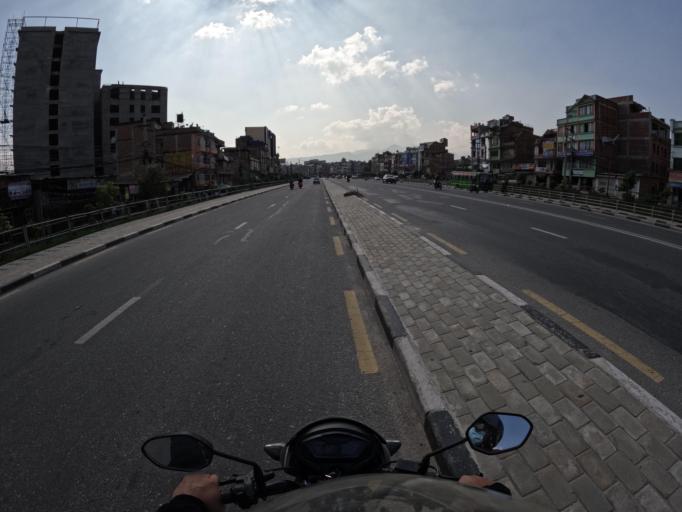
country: NP
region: Central Region
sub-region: Bagmati Zone
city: Patan
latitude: 27.6684
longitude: 85.3348
